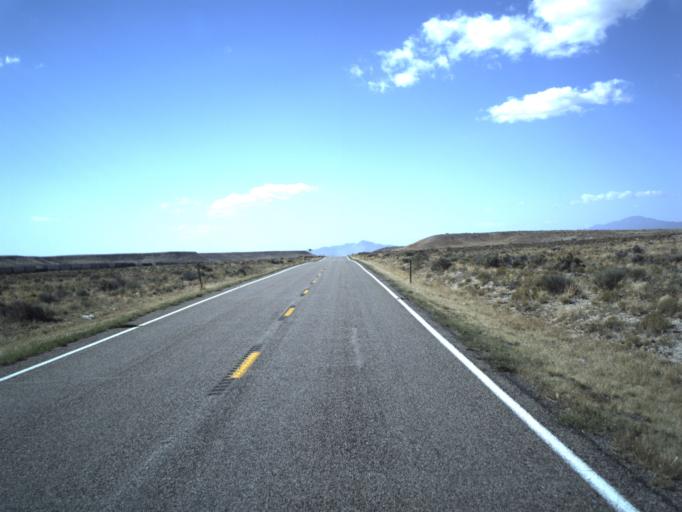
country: US
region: Utah
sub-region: Beaver County
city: Milford
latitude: 38.7556
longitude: -112.9456
